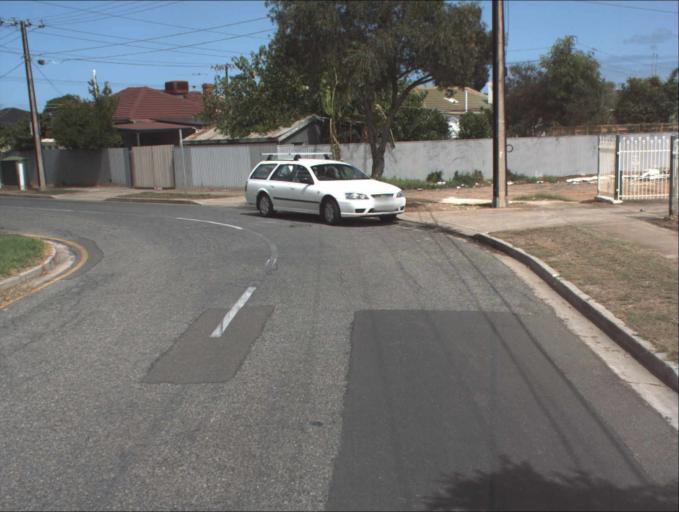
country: AU
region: South Australia
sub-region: Charles Sturt
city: Woodville
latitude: -34.8852
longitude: 138.5661
